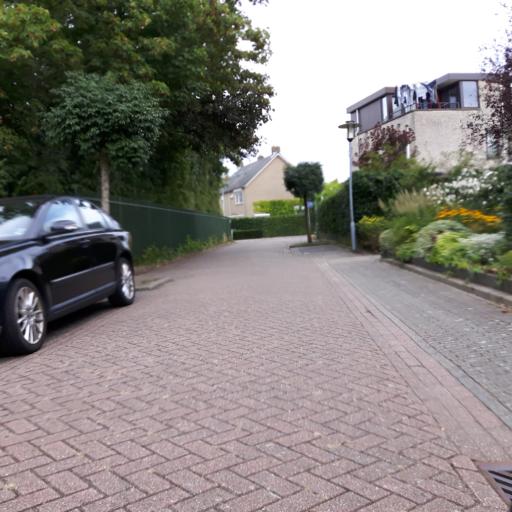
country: NL
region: Zeeland
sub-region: Gemeente Goes
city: Goes
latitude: 51.4952
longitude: 3.8995
